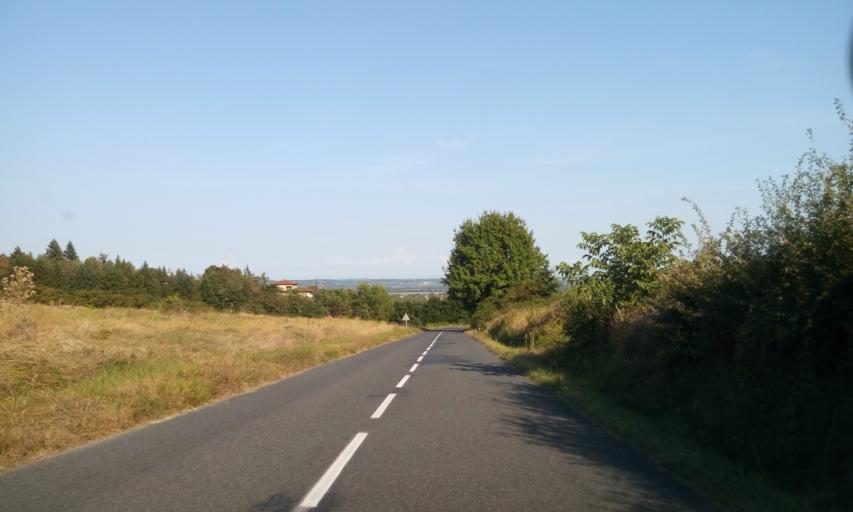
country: FR
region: Rhone-Alpes
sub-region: Departement du Rhone
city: Anse
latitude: 45.9290
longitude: 4.7005
